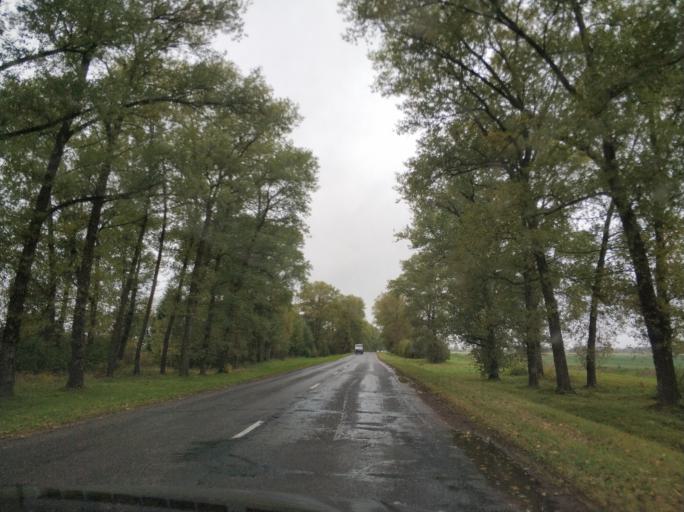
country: BY
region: Vitebsk
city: Polatsk
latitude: 55.4326
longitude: 28.9879
